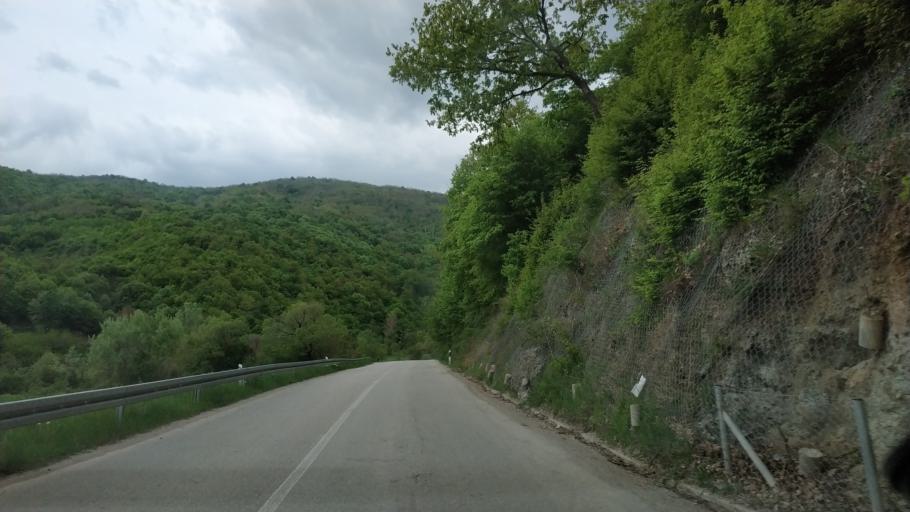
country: RS
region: Central Serbia
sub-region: Nisavski Okrug
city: Aleksinac
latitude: 43.6310
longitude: 21.7154
